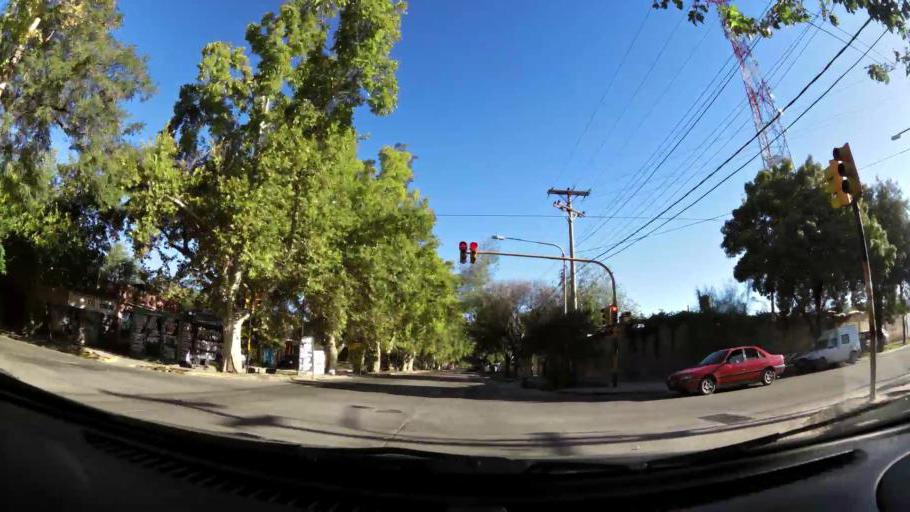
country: AR
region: Mendoza
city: Las Heras
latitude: -32.8540
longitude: -68.8269
